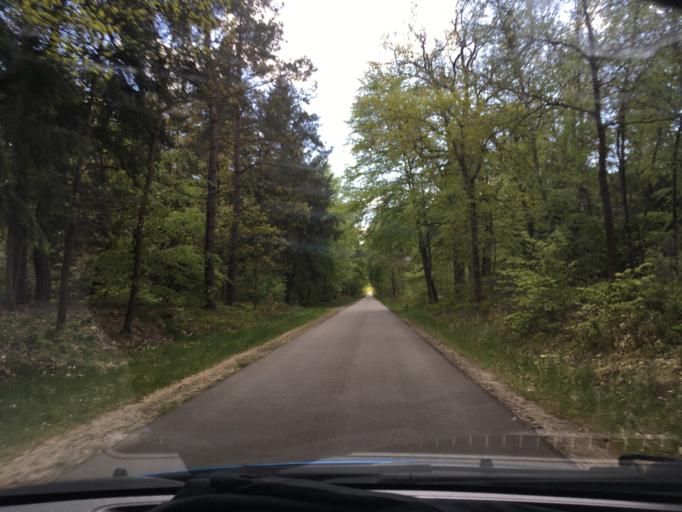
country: DE
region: Lower Saxony
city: Nahrendorf
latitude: 53.1344
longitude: 10.7999
